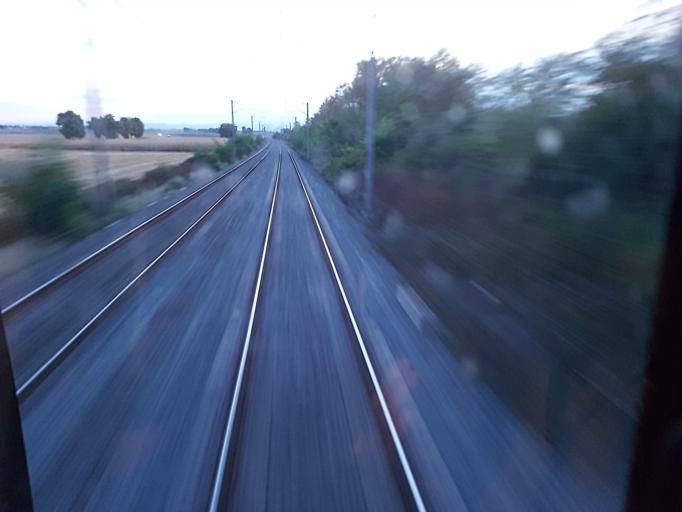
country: FR
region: Auvergne
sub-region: Departement du Puy-de-Dome
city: Ennezat
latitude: 45.9588
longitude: 3.2532
